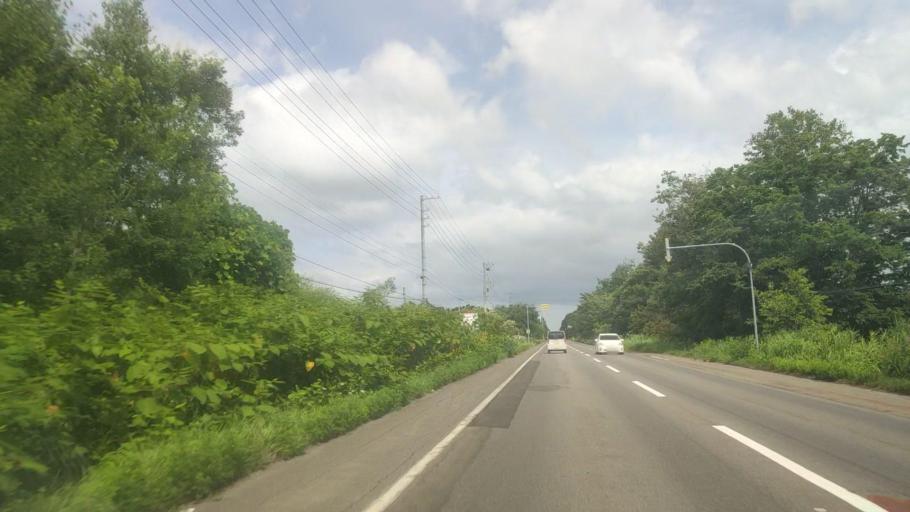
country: JP
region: Hokkaido
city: Nanae
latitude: 42.0270
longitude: 140.6117
